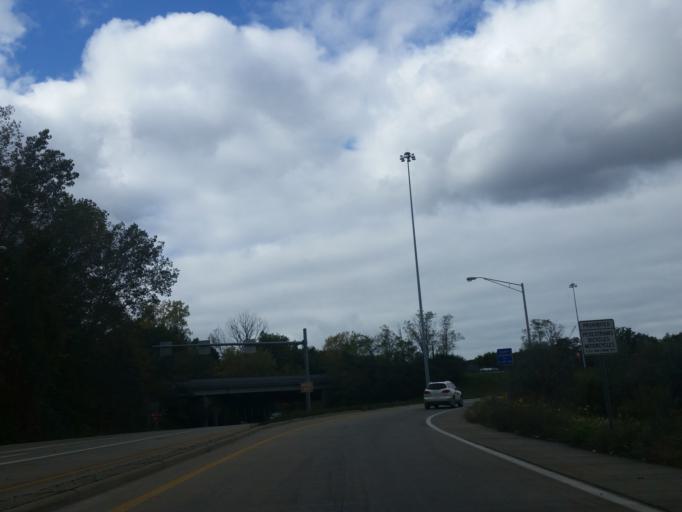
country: US
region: Ohio
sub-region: Cuyahoga County
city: Newburgh Heights
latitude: 41.4542
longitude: -81.6891
